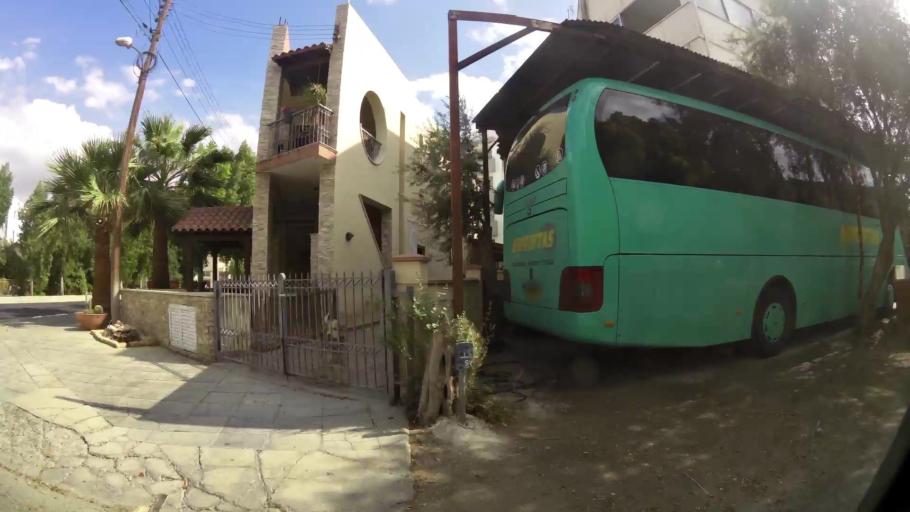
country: CY
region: Lefkosia
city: Nicosia
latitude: 35.1888
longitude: 33.3825
